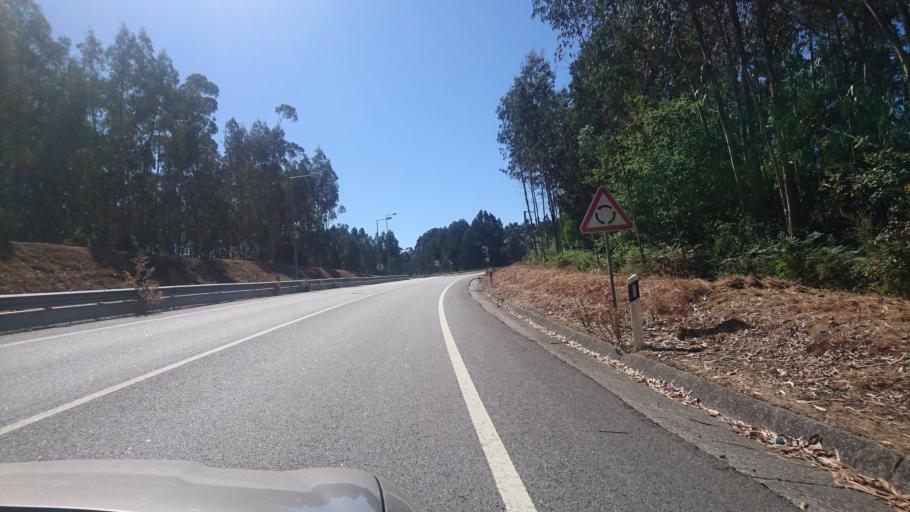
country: PT
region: Aveiro
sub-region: Santa Maria da Feira
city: Arrifana
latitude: 40.9254
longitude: -8.4897
